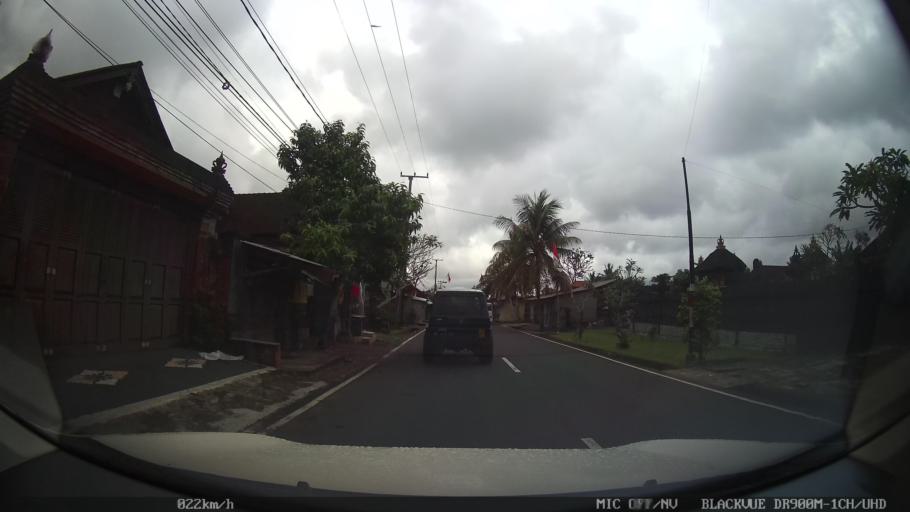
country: ID
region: Bali
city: Banjar Sayanbaleran
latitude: -8.5161
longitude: 115.1874
